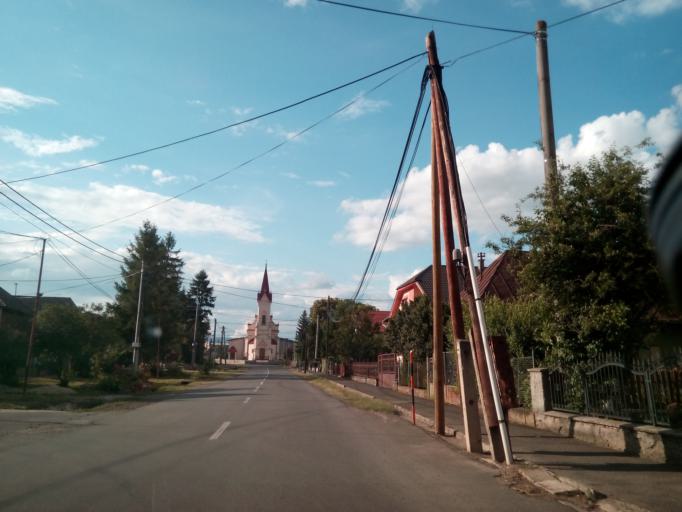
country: SK
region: Kosicky
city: Secovce
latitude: 48.5805
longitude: 21.5700
